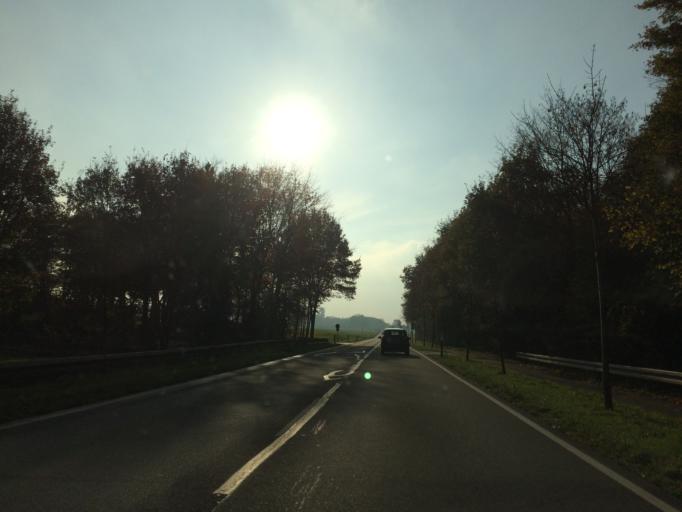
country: DE
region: North Rhine-Westphalia
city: Dorsten
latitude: 51.6836
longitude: 6.9896
